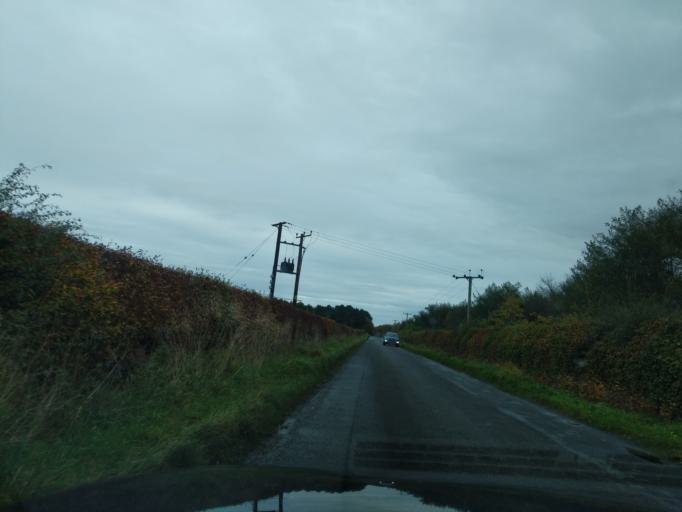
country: GB
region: Scotland
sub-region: Fife
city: Saint Andrews
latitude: 56.2882
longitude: -2.8120
